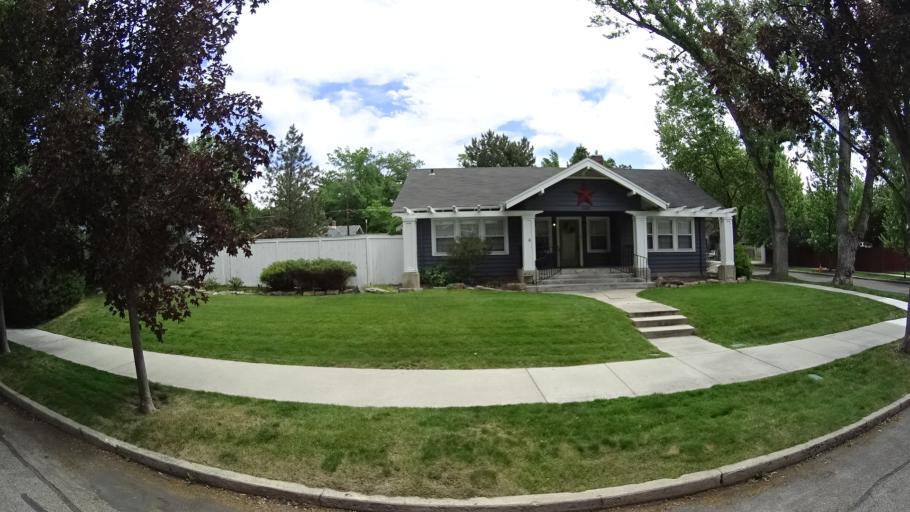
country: US
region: Idaho
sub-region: Ada County
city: Boise
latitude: 43.6294
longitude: -116.2169
